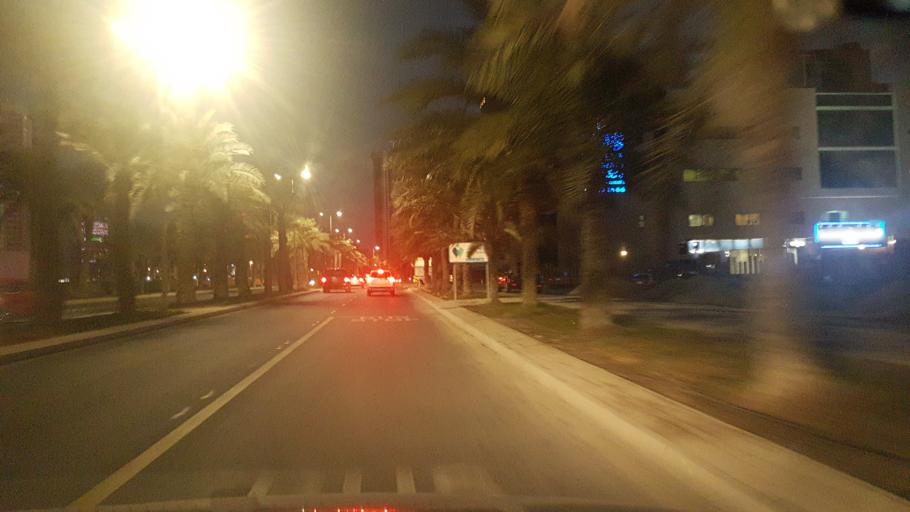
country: BH
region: Manama
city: Jidd Hafs
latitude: 26.2377
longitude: 50.5426
